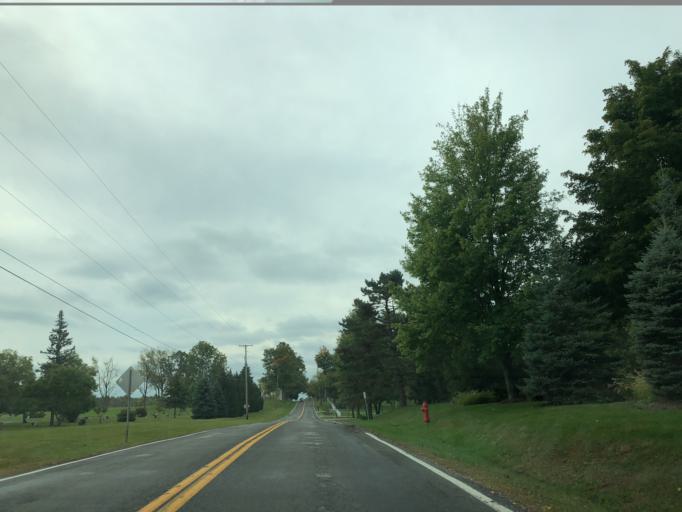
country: US
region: Ohio
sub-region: Summit County
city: Boston Heights
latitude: 41.2907
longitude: -81.5390
